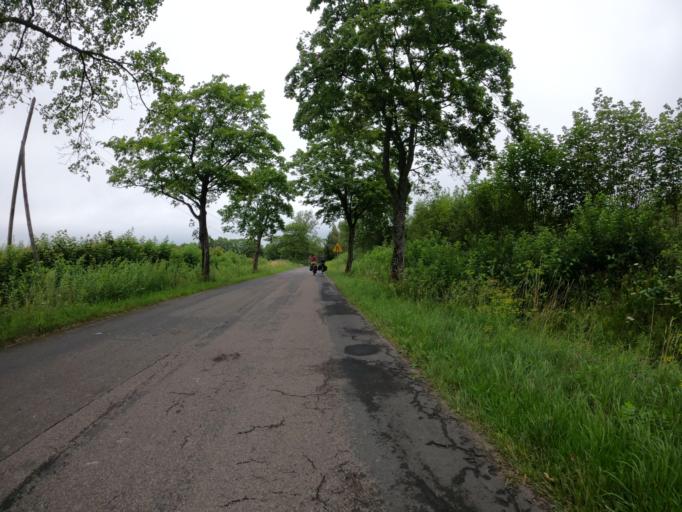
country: PL
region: West Pomeranian Voivodeship
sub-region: Powiat szczecinecki
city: Grzmiaca
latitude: 53.8951
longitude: 16.5021
